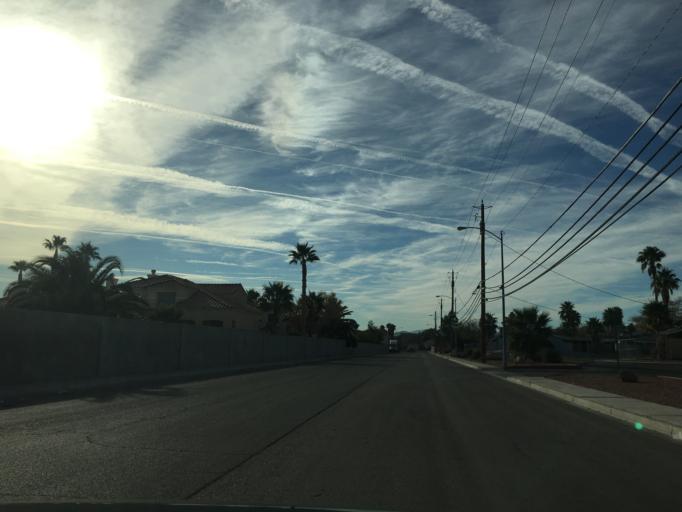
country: US
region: Nevada
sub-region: Clark County
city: Enterprise
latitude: 36.0194
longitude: -115.1679
